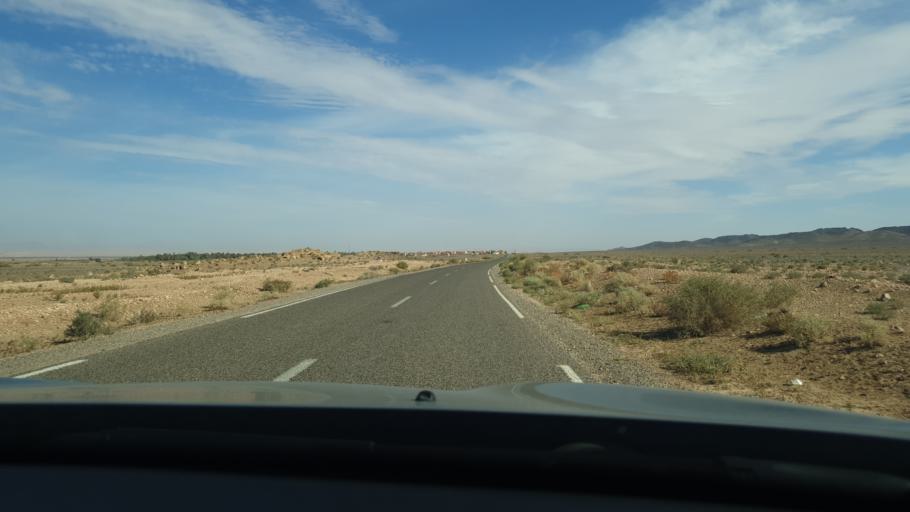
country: MA
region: Meknes-Tafilalet
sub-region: Errachidia
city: Goulmima
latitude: 31.5157
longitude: -4.9834
